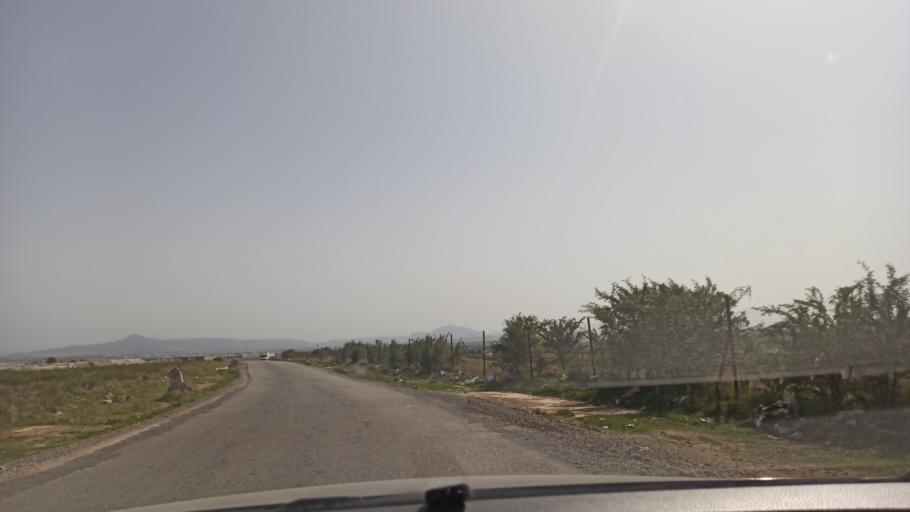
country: TN
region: Manouba
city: Manouba
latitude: 36.7345
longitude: 10.0910
